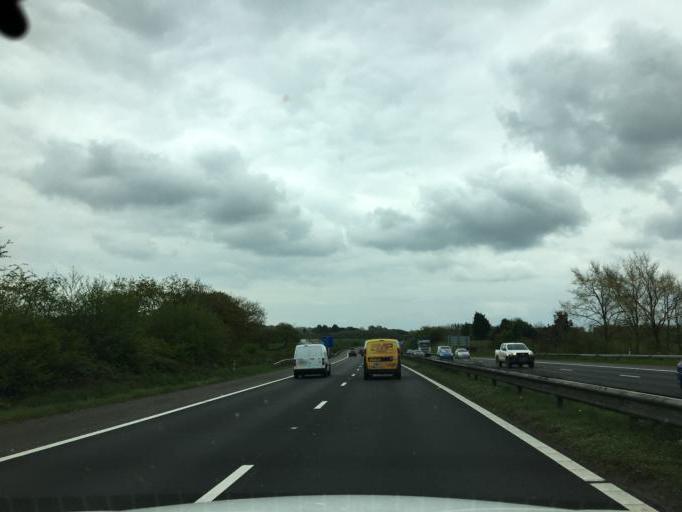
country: GB
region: Wales
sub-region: City and County of Swansea
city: Pontarddulais
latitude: 51.7066
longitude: -4.0492
